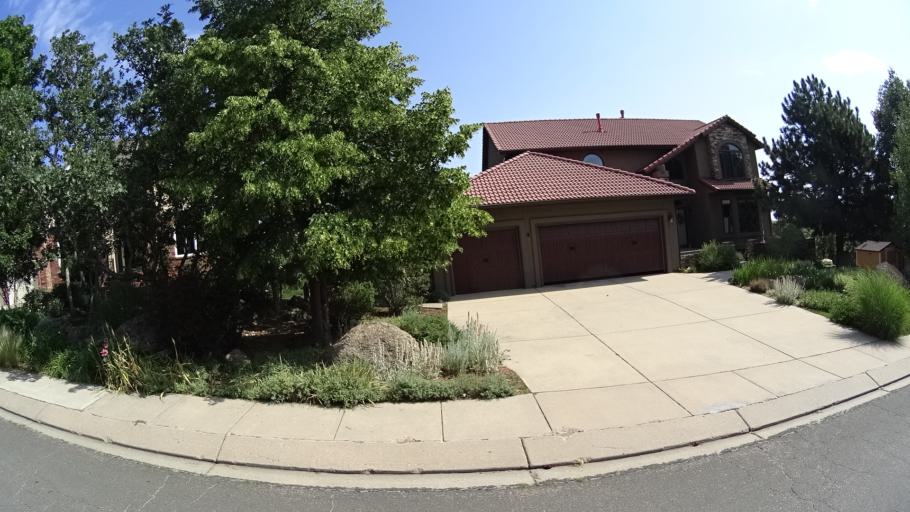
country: US
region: Colorado
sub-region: El Paso County
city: Fort Carson
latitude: 38.7515
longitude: -104.8342
